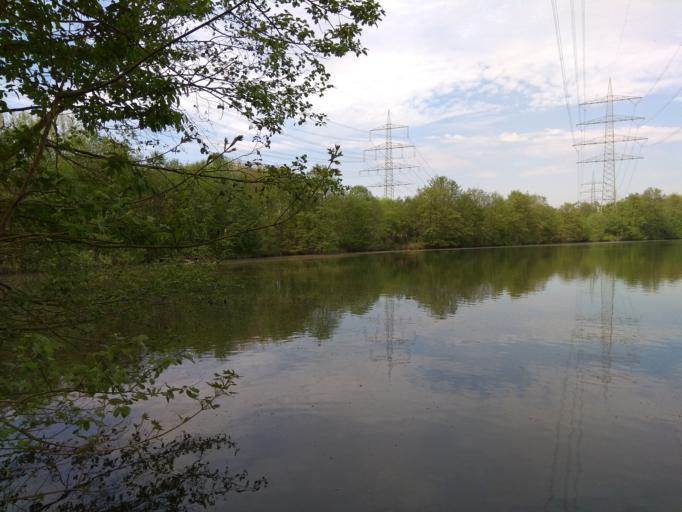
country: DE
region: North Rhine-Westphalia
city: Herten
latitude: 51.5679
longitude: 7.1339
